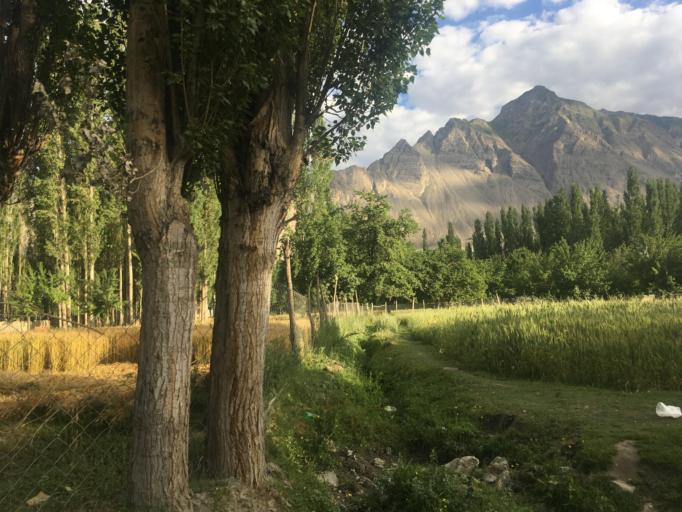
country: PK
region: Gilgit-Baltistan
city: Skardu
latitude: 35.2960
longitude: 75.6189
